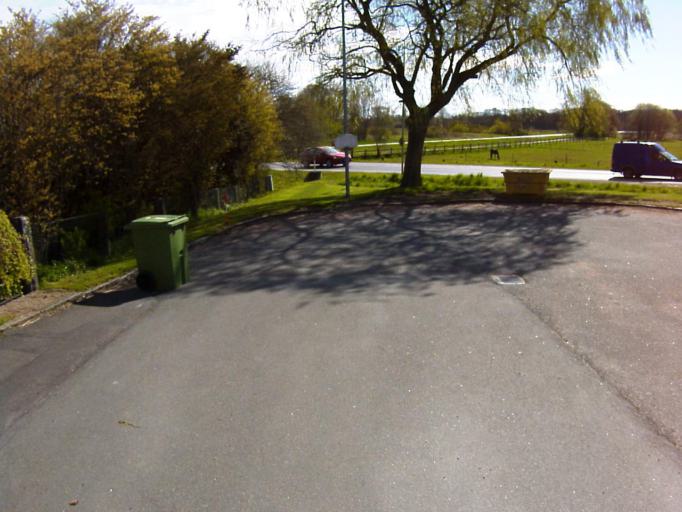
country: SE
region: Skane
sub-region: Kristianstads Kommun
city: Norra Asum
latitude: 55.9909
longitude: 14.1541
